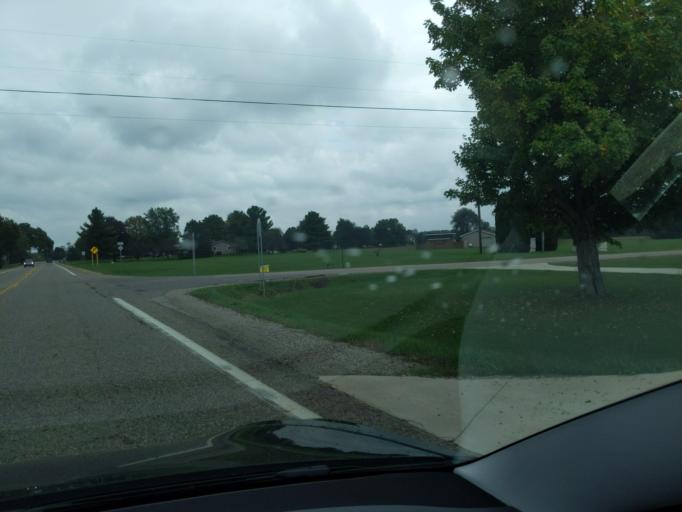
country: US
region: Michigan
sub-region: Eaton County
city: Charlotte
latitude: 42.5522
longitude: -84.7884
